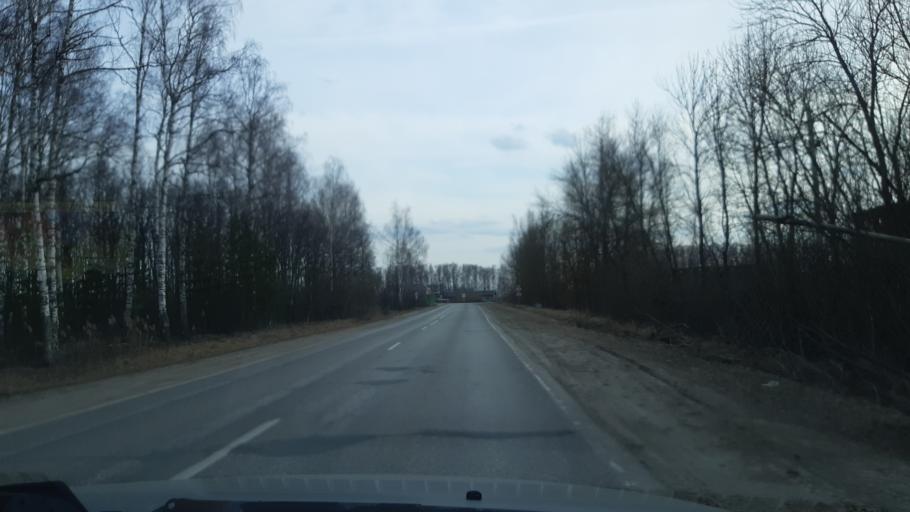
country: RU
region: Vladimir
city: Luknovo
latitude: 56.2257
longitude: 42.0348
